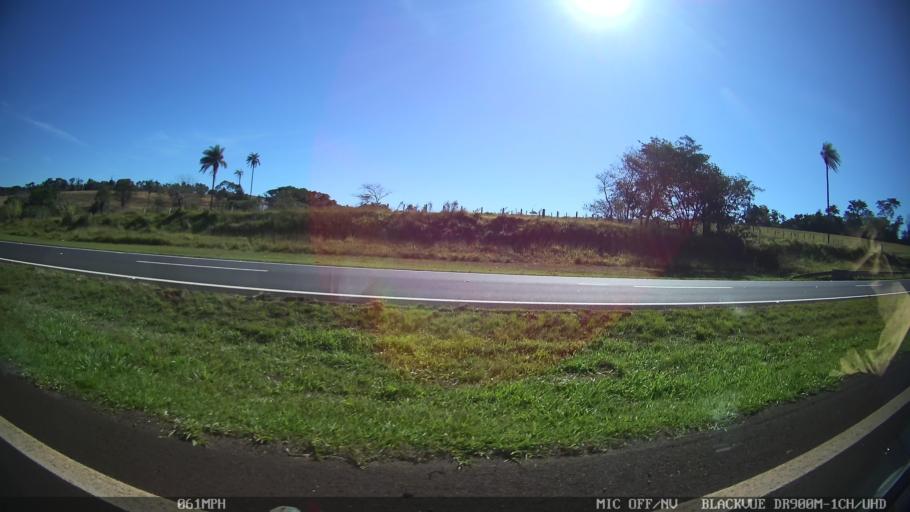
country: BR
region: Sao Paulo
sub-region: Franca
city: Franca
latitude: -20.5760
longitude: -47.3579
